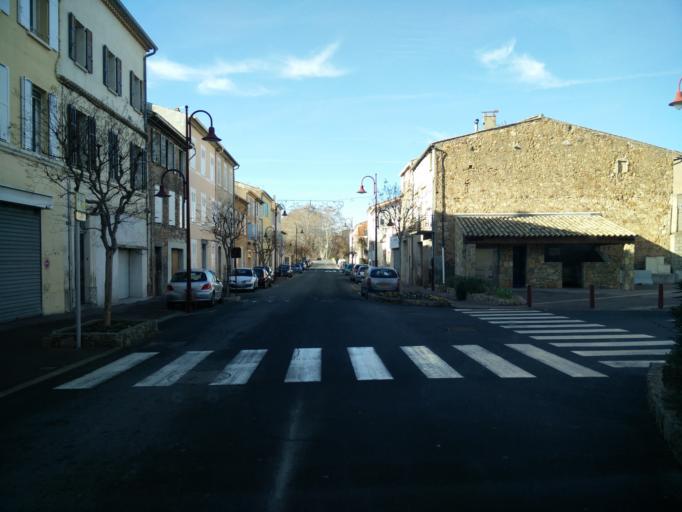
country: FR
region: Provence-Alpes-Cote d'Azur
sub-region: Departement du Var
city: Vidauban
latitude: 43.4275
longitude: 6.4306
